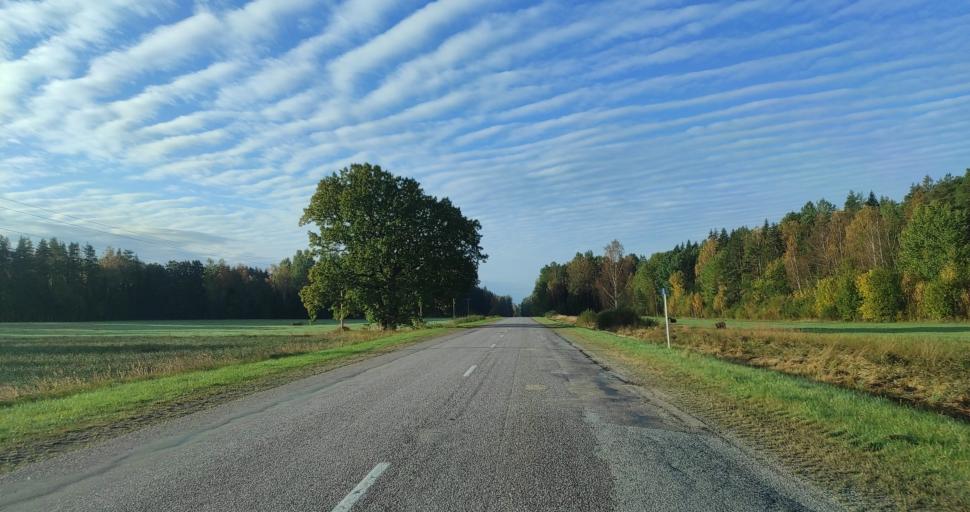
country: LV
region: Skrunda
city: Skrunda
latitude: 56.8024
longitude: 22.0080
